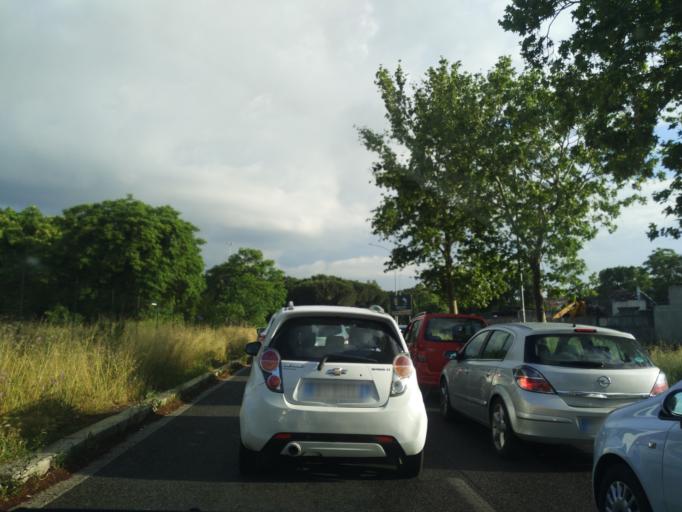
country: IT
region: Latium
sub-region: Citta metropolitana di Roma Capitale
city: Rome
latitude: 41.8965
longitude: 12.5745
